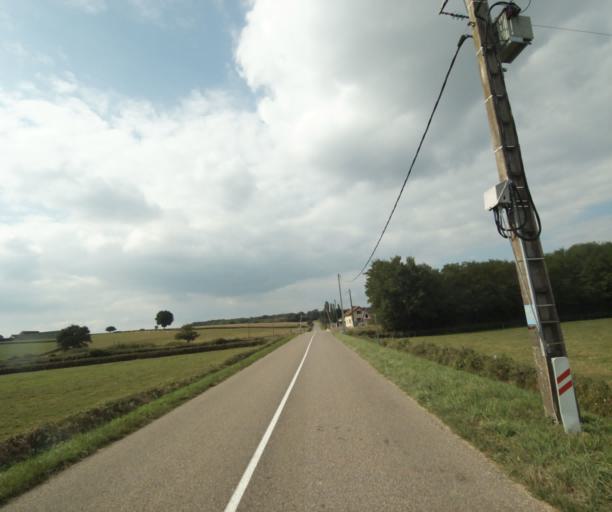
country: FR
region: Bourgogne
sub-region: Departement de Saone-et-Loire
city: Palinges
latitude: 46.5084
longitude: 4.1832
